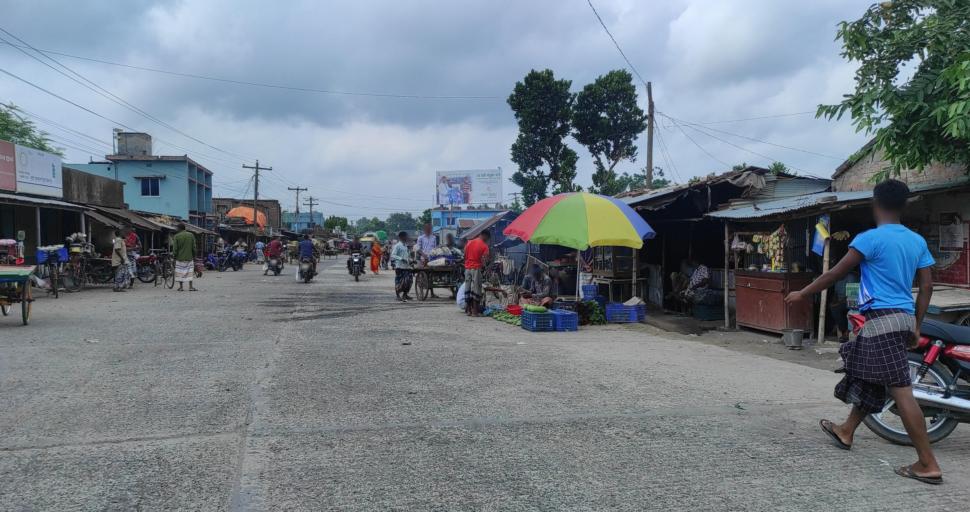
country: BD
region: Rajshahi
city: Shibganj
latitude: 24.8362
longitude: 88.1417
